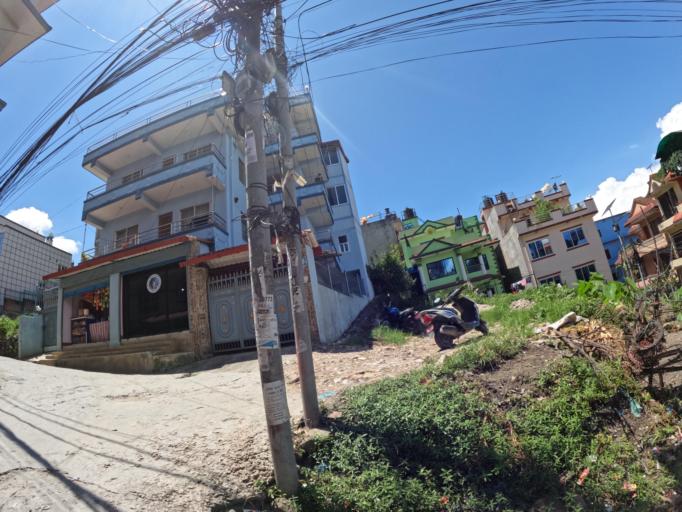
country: NP
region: Central Region
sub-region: Bagmati Zone
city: Kathmandu
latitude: 27.7450
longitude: 85.3259
